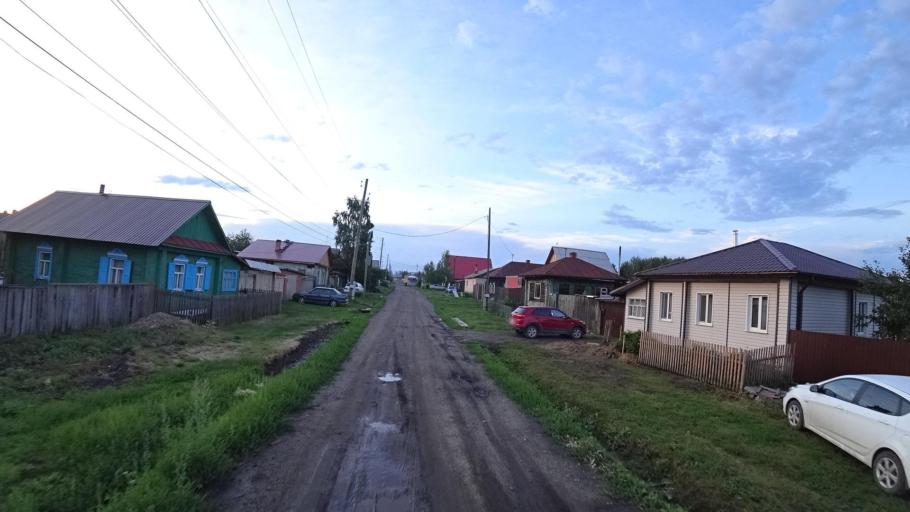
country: RU
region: Sverdlovsk
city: Kamyshlov
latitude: 56.8596
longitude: 62.7135
